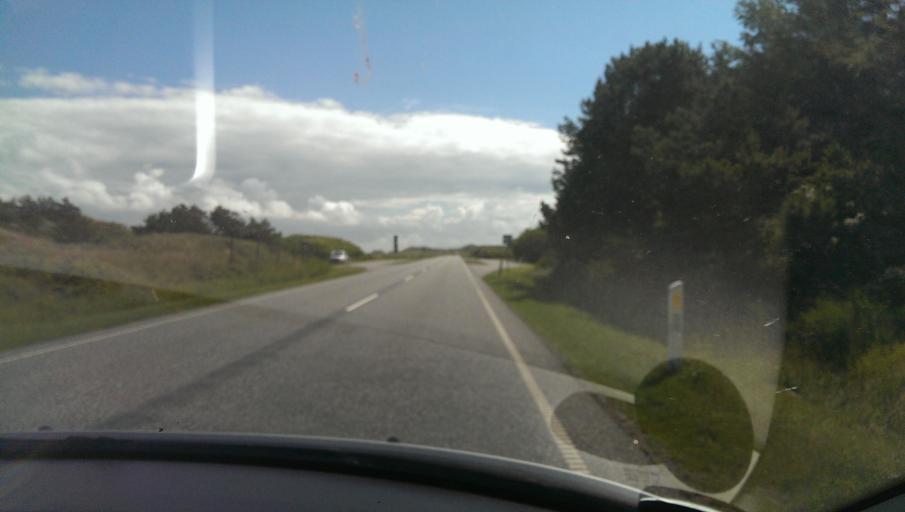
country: DK
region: Central Jutland
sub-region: Holstebro Kommune
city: Ulfborg
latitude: 56.2428
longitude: 8.1392
